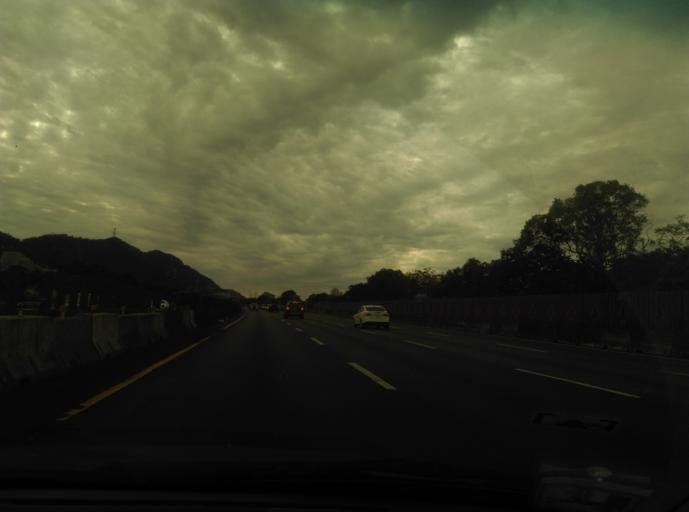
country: TW
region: Taiwan
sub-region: Taoyuan
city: Taoyuan
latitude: 24.9476
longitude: 121.3704
